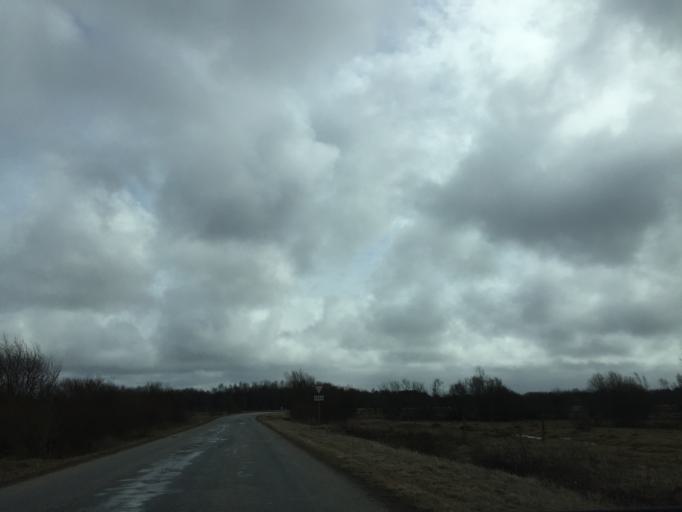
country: EE
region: Laeaene
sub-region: Lihula vald
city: Lihula
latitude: 58.7258
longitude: 23.9135
